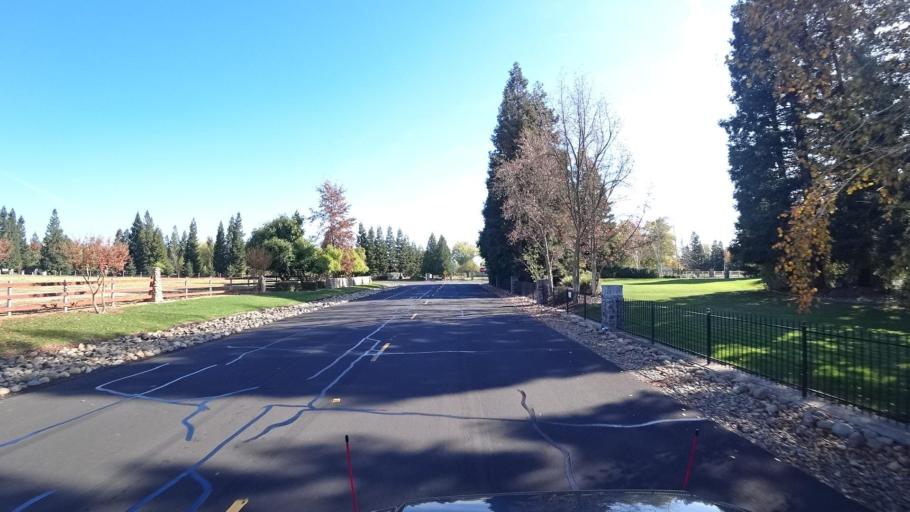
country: US
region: California
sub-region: Sacramento County
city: Wilton
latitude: 38.4317
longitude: -121.2833
